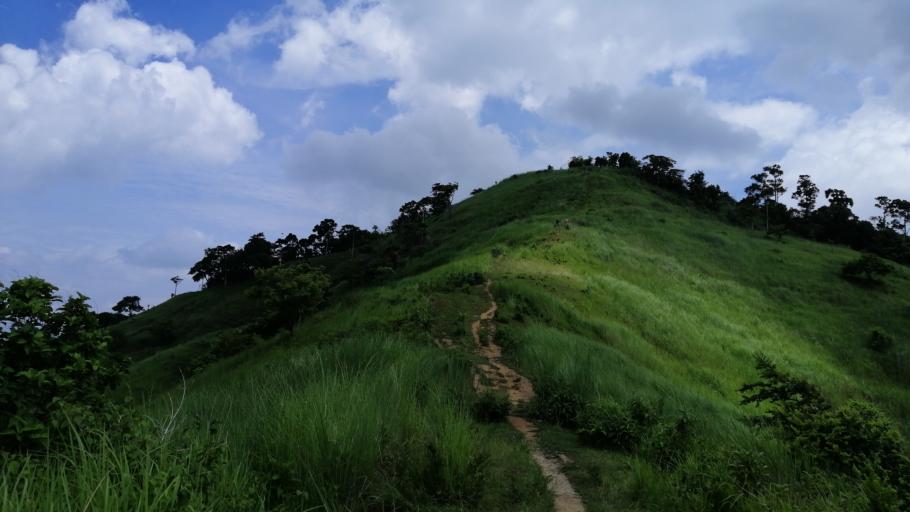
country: PH
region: Central Luzon
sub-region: Province of Bulacan
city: Sibul
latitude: 15.1467
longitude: 121.1402
